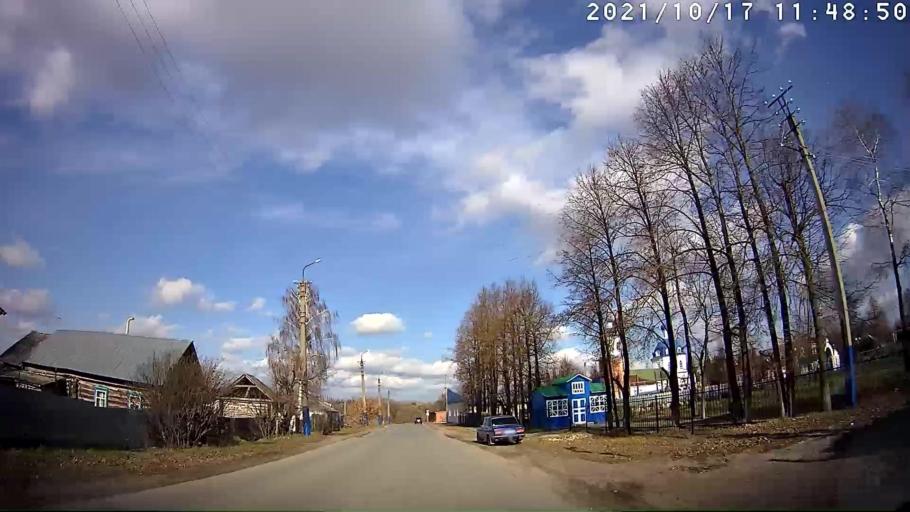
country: RU
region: Mariy-El
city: Kuzhener
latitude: 57.0046
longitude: 48.7346
